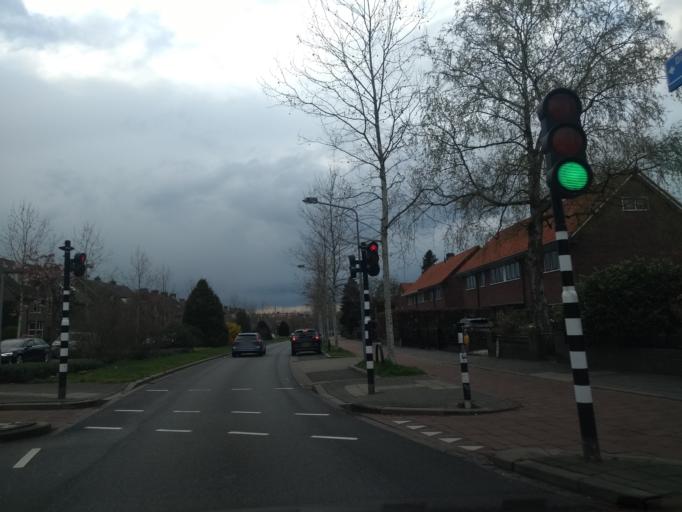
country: NL
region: North Holland
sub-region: Gemeente Hilversum
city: Hilversum
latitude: 52.2119
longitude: 5.1622
